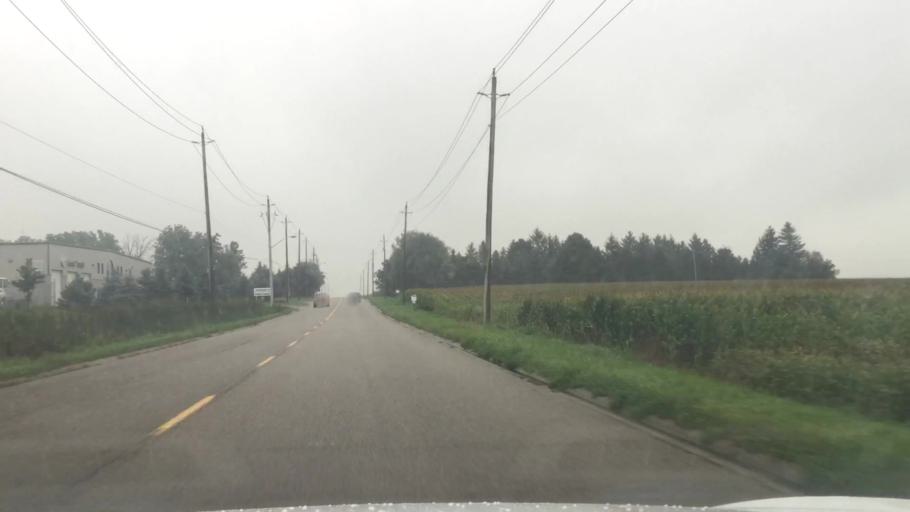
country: CA
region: Ontario
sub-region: Oxford County
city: Woodstock
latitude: 43.1100
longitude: -80.7225
